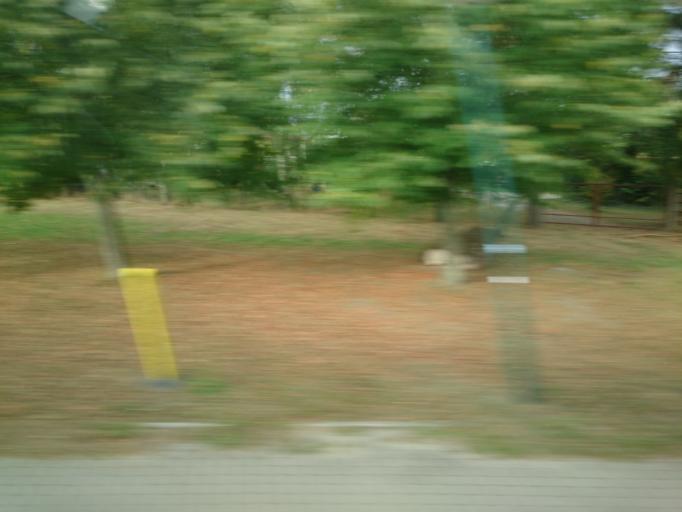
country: DE
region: Mecklenburg-Vorpommern
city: Pasewalk
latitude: 53.5224
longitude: 13.9765
